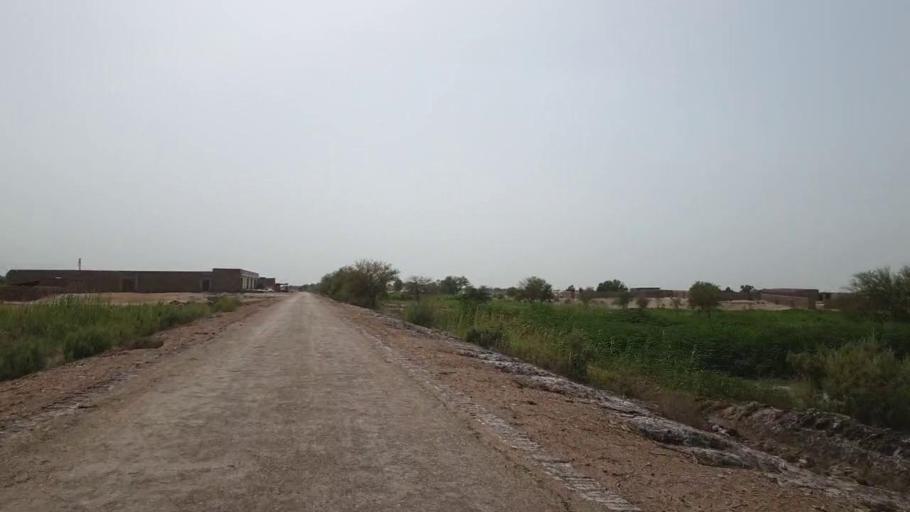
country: PK
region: Sindh
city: Bandhi
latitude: 26.5386
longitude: 68.3974
